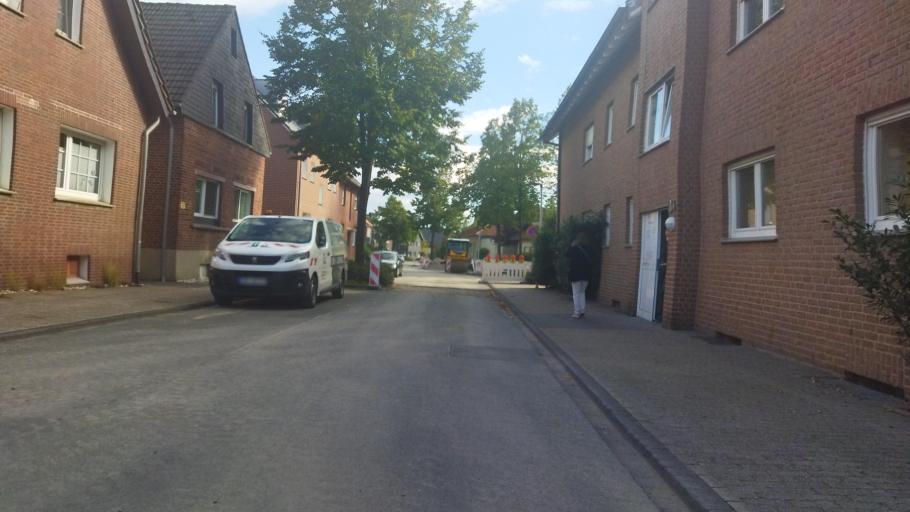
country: DE
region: North Rhine-Westphalia
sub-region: Regierungsbezirk Munster
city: Dulmen
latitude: 51.8362
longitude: 7.2745
